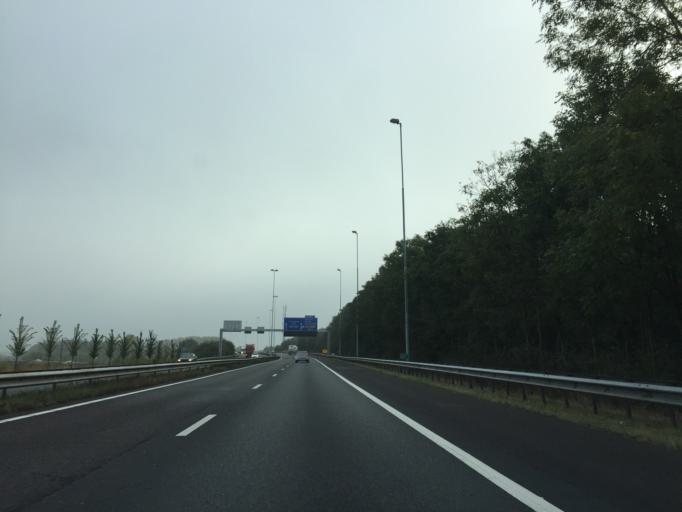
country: NL
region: South Holland
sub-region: Gemeente Giessenlanden
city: Giessenburg
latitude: 51.8391
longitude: 4.9225
